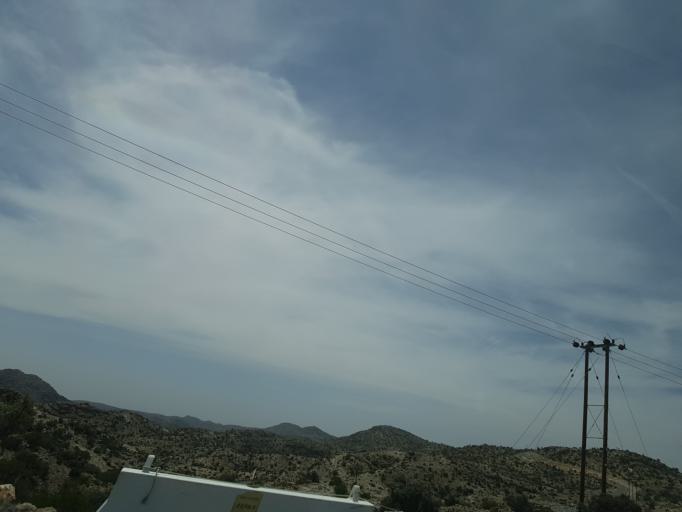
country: OM
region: Muhafazat ad Dakhiliyah
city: Nizwa
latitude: 23.1140
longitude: 57.6475
